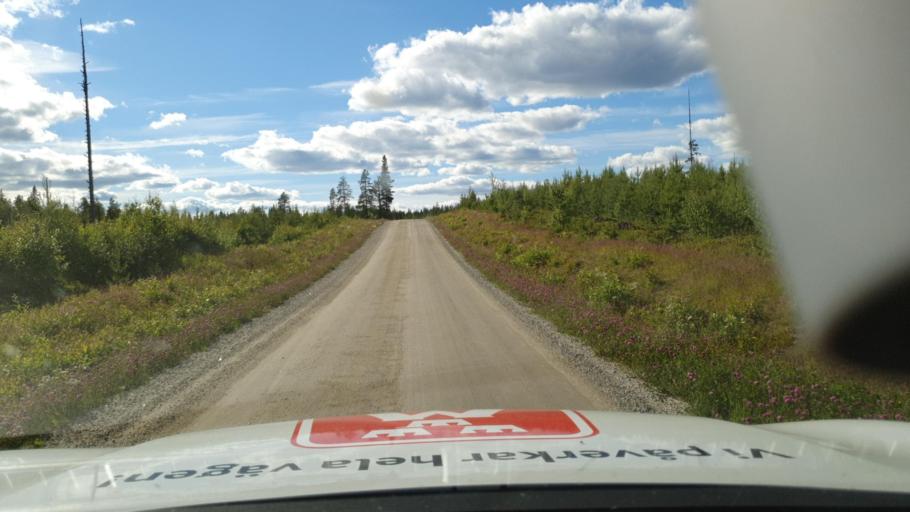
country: SE
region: Vaesterbotten
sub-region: Lycksele Kommun
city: Lycksele
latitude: 64.4036
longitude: 18.5578
